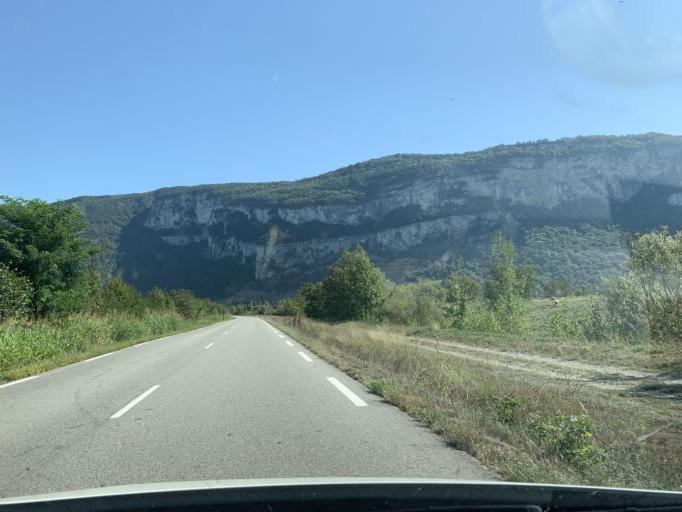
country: FR
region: Rhone-Alpes
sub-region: Departement de la Savoie
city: Saint-Genix-sur-Guiers
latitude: 45.6399
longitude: 5.6704
